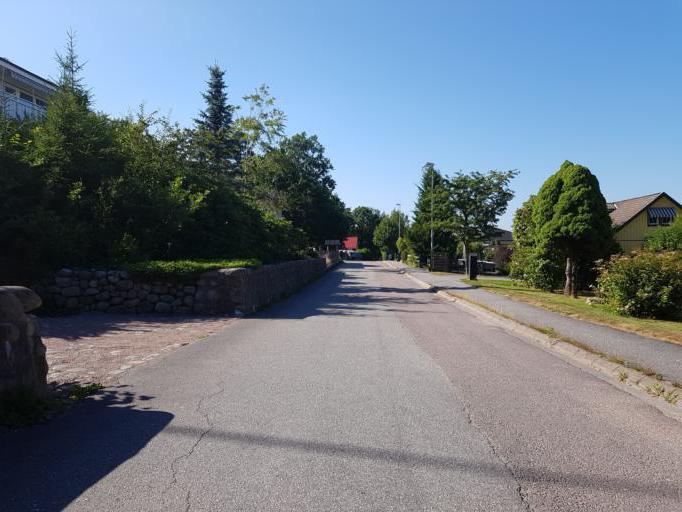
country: SE
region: Vaestra Goetaland
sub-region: Partille Kommun
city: Furulund
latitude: 57.7057
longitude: 12.1410
